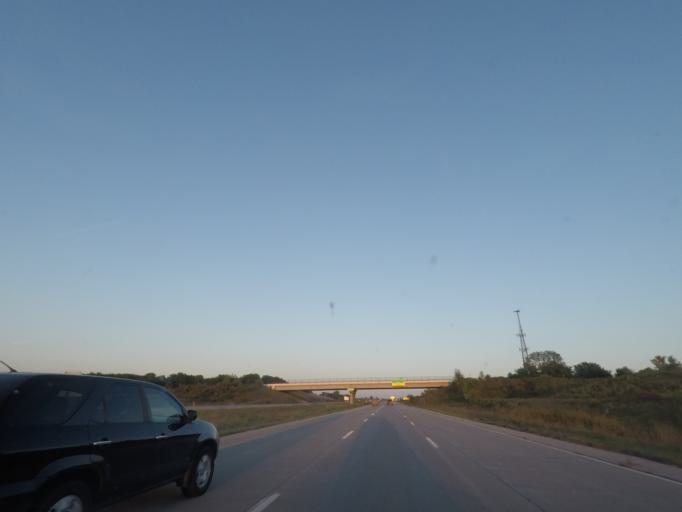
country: US
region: Iowa
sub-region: Polk County
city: West Des Moines
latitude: 41.5224
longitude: -93.7391
